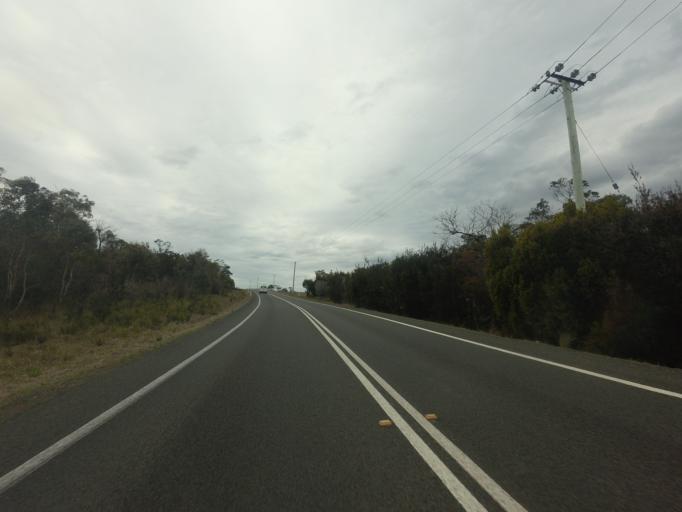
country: AU
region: Tasmania
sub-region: Break O'Day
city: St Helens
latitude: -42.0821
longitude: 148.0686
